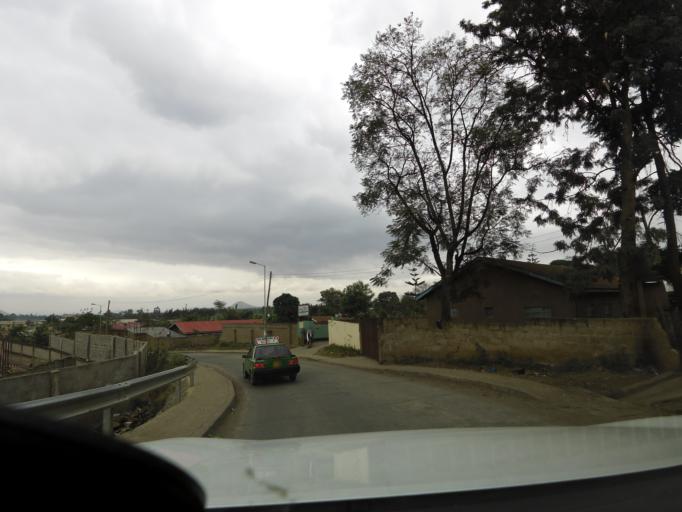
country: TZ
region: Arusha
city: Arusha
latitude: -3.3673
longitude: 36.6607
